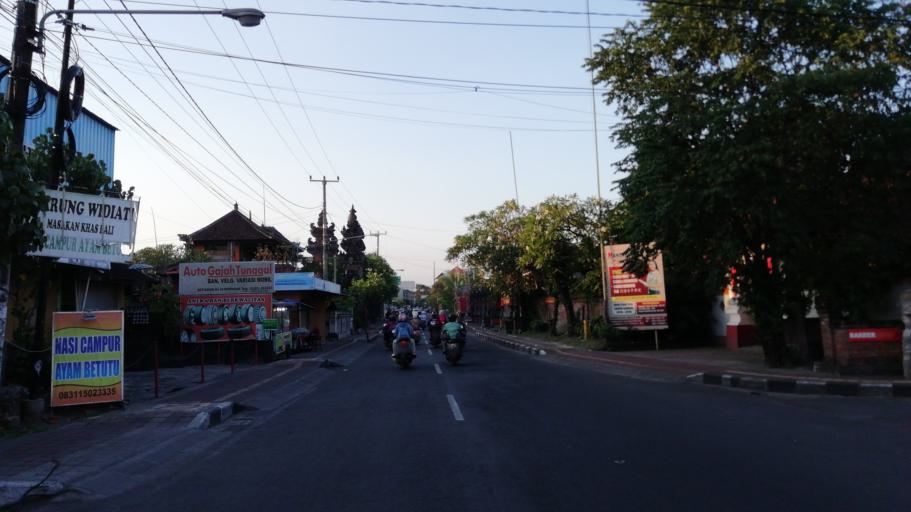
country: ID
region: Bali
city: Denpasar
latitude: -8.6521
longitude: 115.2087
